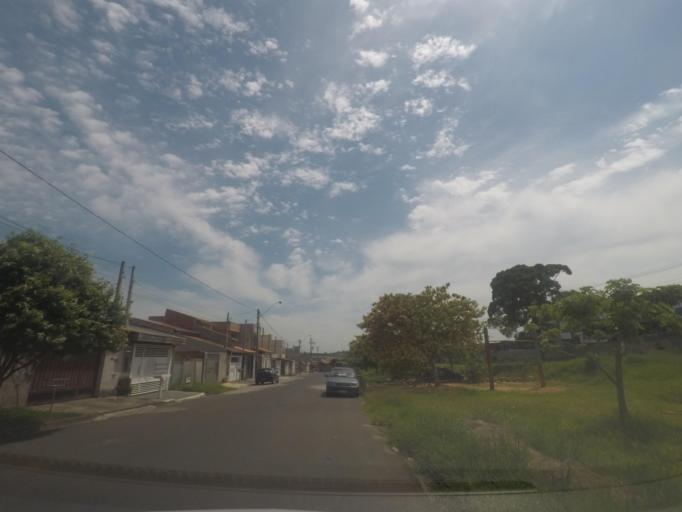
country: BR
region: Sao Paulo
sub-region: Sumare
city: Sumare
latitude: -22.8035
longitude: -47.2634
